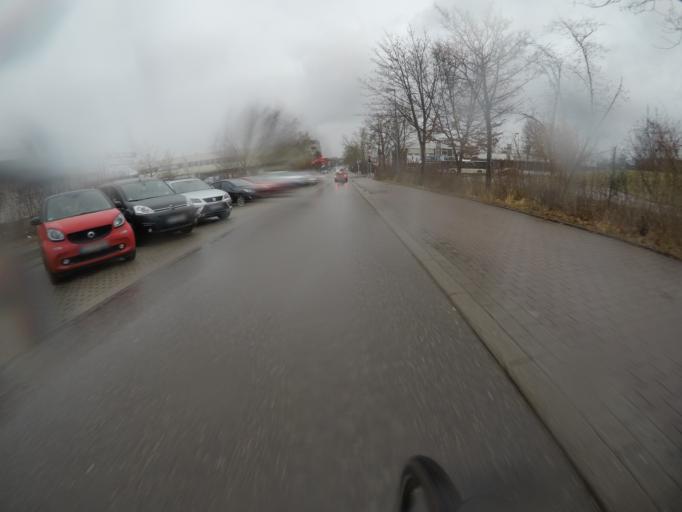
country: DE
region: Baden-Wuerttemberg
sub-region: Regierungsbezirk Stuttgart
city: Boeblingen
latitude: 48.6803
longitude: 8.9814
